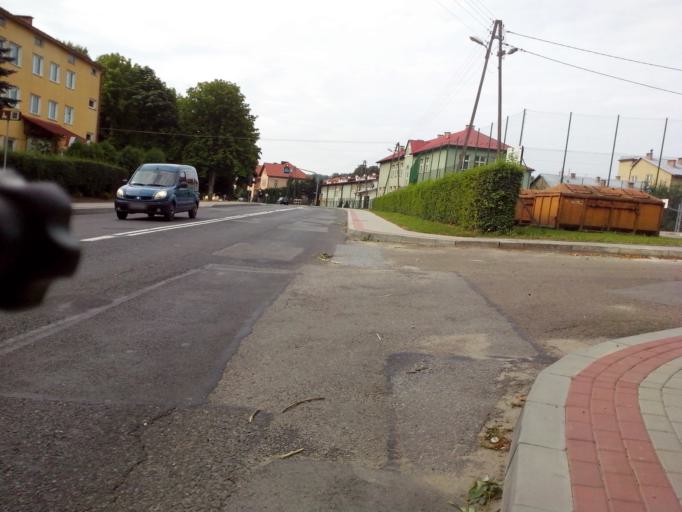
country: PL
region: Subcarpathian Voivodeship
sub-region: Powiat brzozowski
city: Domaradz
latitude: 49.7902
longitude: 21.9452
